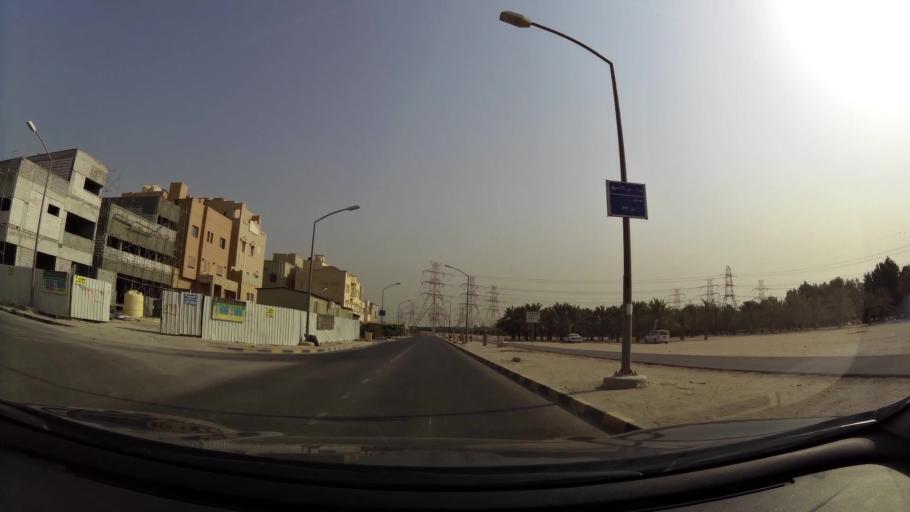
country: KW
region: Mubarak al Kabir
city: Sabah as Salim
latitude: 29.2743
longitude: 48.0396
